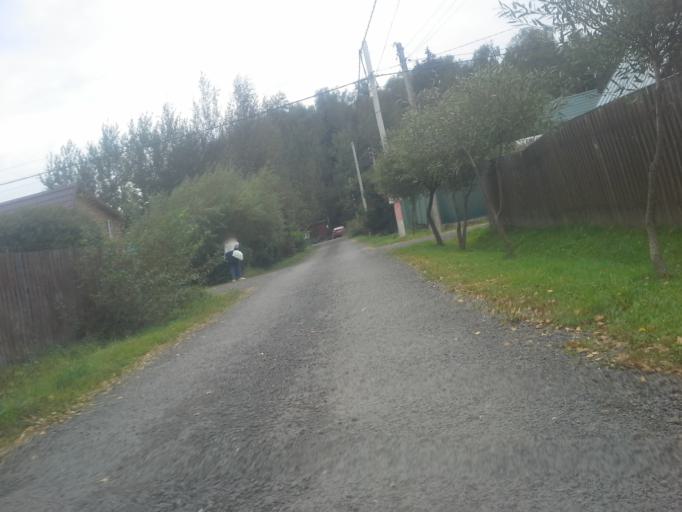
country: RU
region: Moskovskaya
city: Kievskij
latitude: 55.4271
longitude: 36.8883
